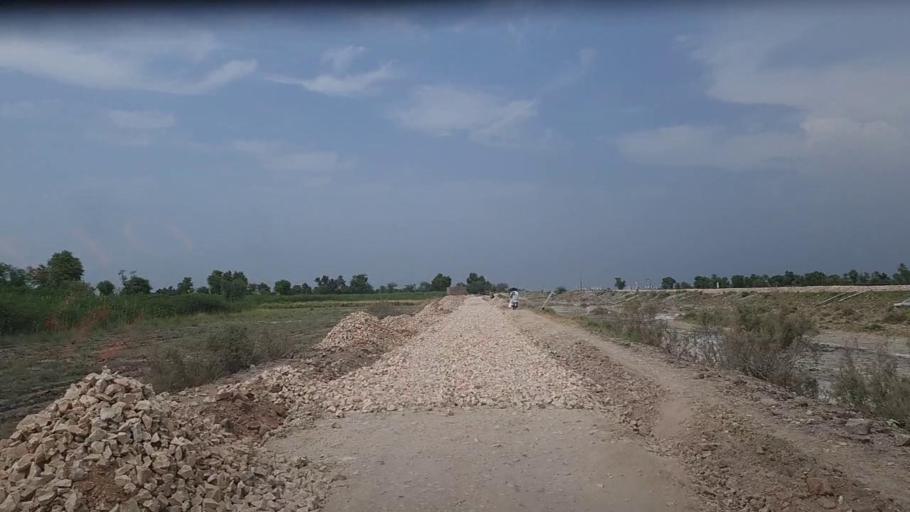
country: PK
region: Sindh
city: Bhiria
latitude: 26.9181
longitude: 68.2961
